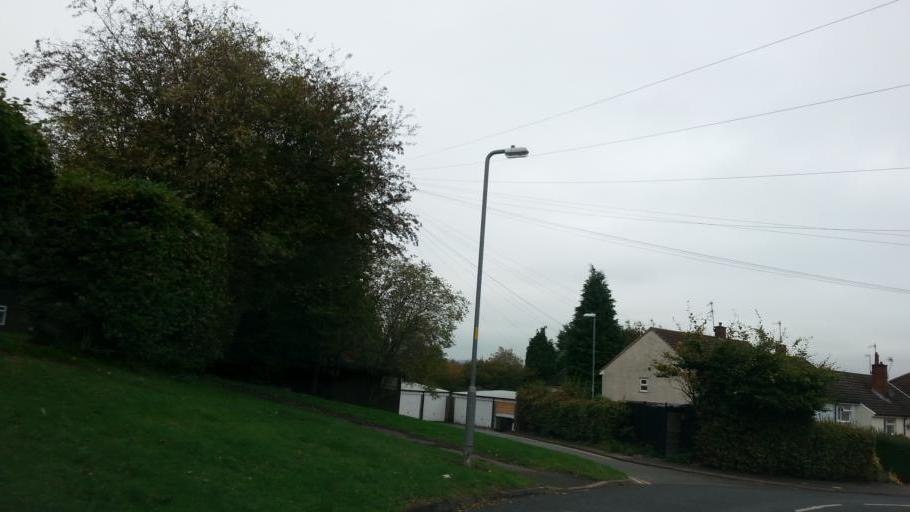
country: GB
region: England
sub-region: Worcestershire
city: Bromsgrove
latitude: 52.3231
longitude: -2.0734
